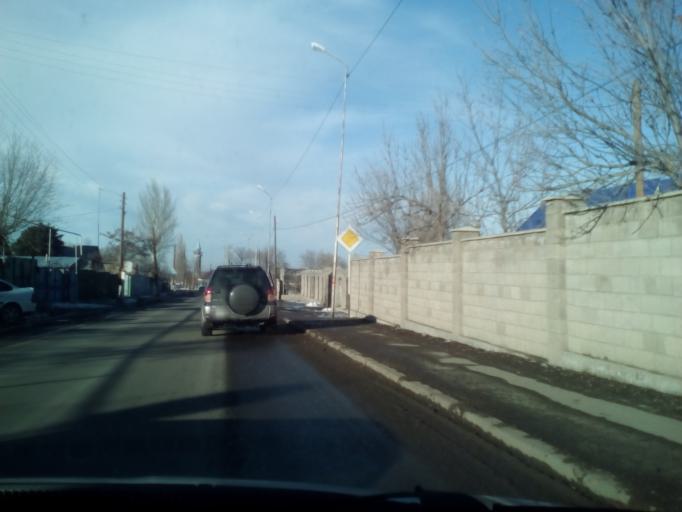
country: KZ
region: Almaty Oblysy
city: Burunday
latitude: 43.1744
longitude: 76.4153
